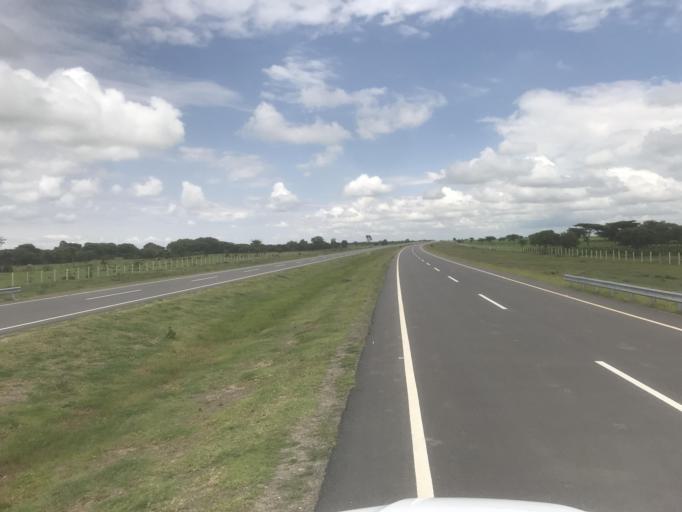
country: ET
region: Oromiya
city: Ziway
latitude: 8.2324
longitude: 38.8745
